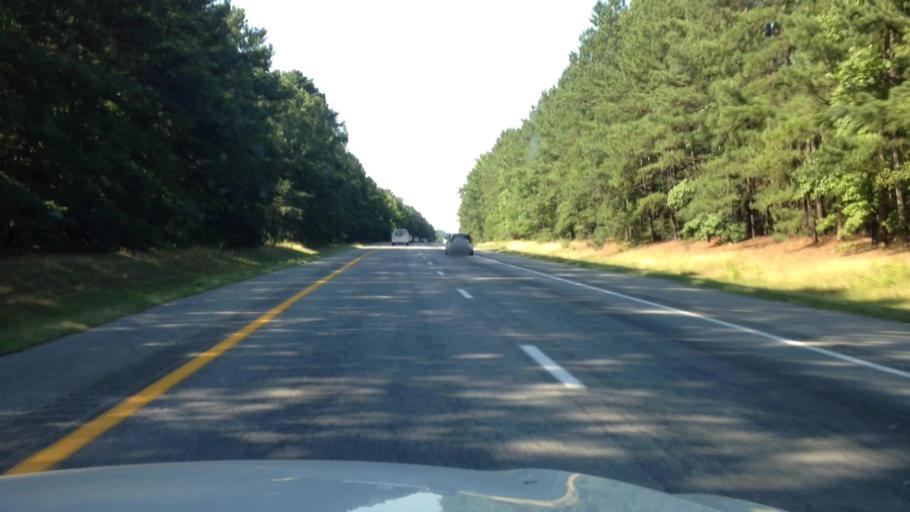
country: US
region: Virginia
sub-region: City of Emporia
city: Emporia
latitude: 36.7935
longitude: -77.4611
